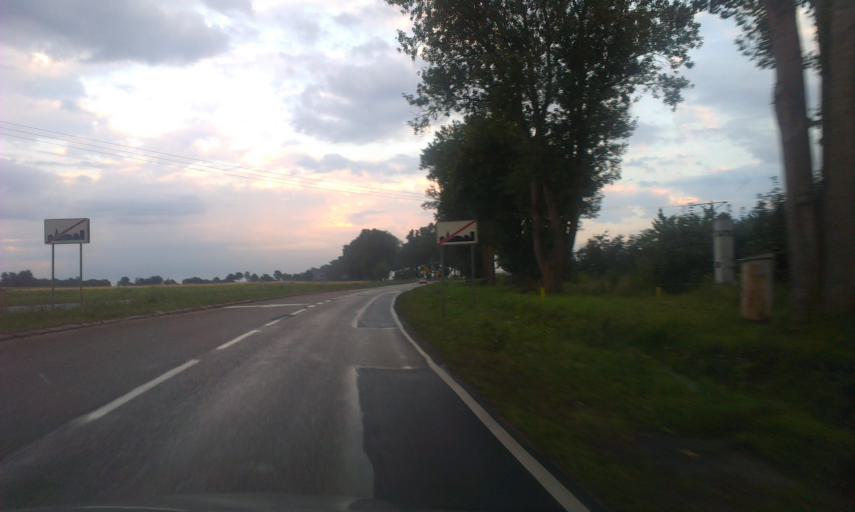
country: PL
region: West Pomeranian Voivodeship
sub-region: Koszalin
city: Koszalin
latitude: 54.1620
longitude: 16.2229
